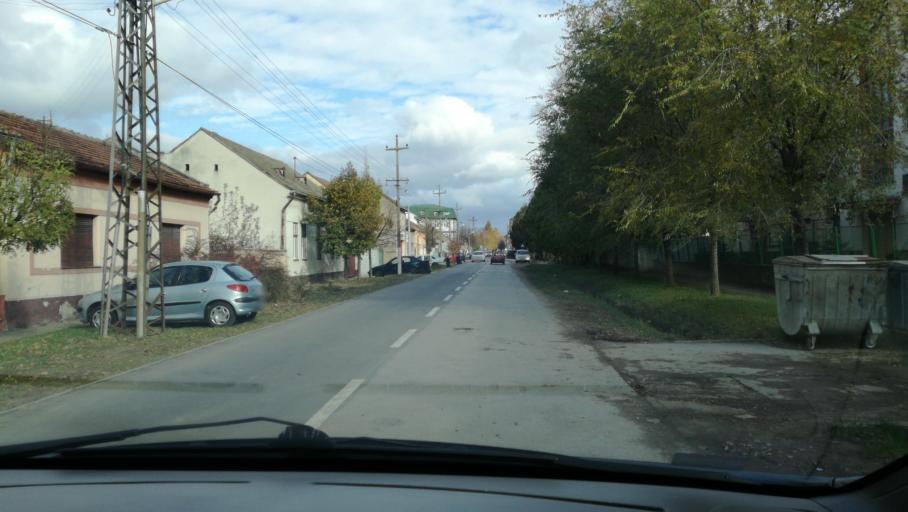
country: RS
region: Autonomna Pokrajina Vojvodina
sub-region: Severnobanatski Okrug
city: Kikinda
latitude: 45.8262
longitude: 20.4569
